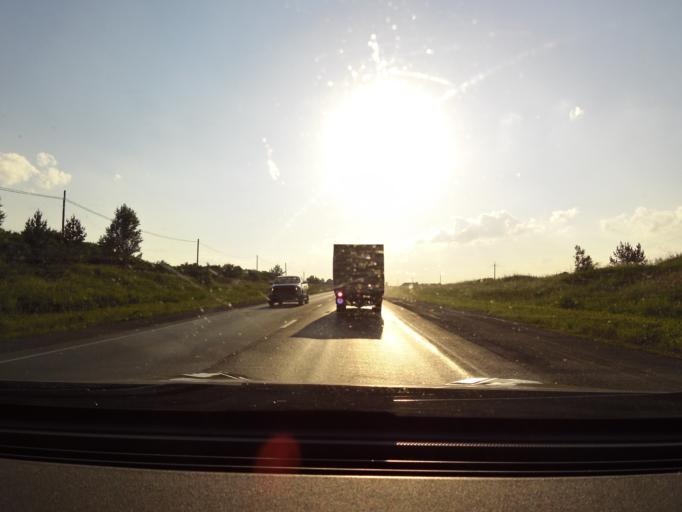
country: RU
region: Sverdlovsk
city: Druzhinino
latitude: 56.8098
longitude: 59.5377
